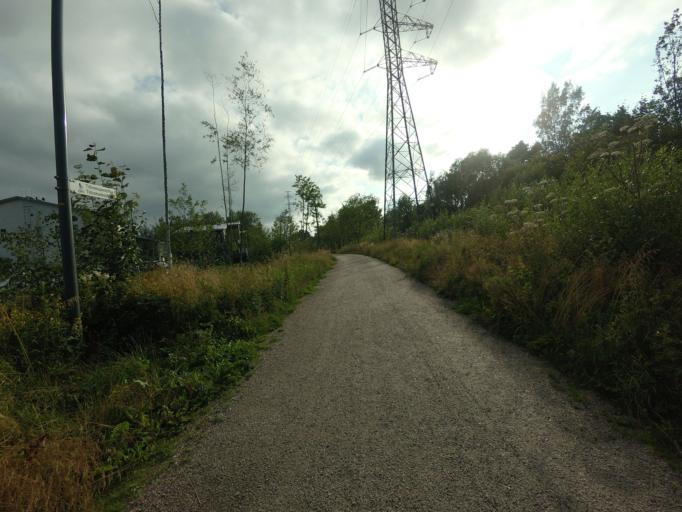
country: FI
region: Uusimaa
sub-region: Helsinki
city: Espoo
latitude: 60.1687
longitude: 24.6383
